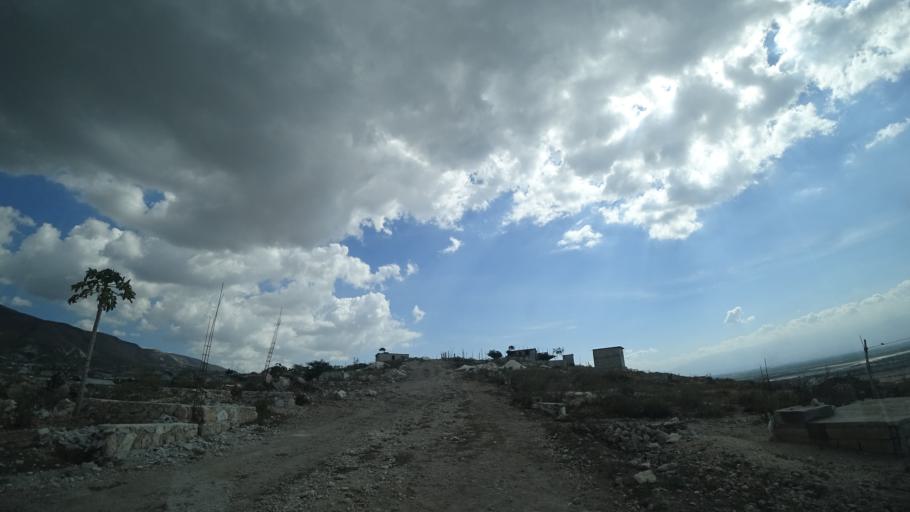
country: HT
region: Ouest
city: Cabaret
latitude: 18.6787
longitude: -72.3137
